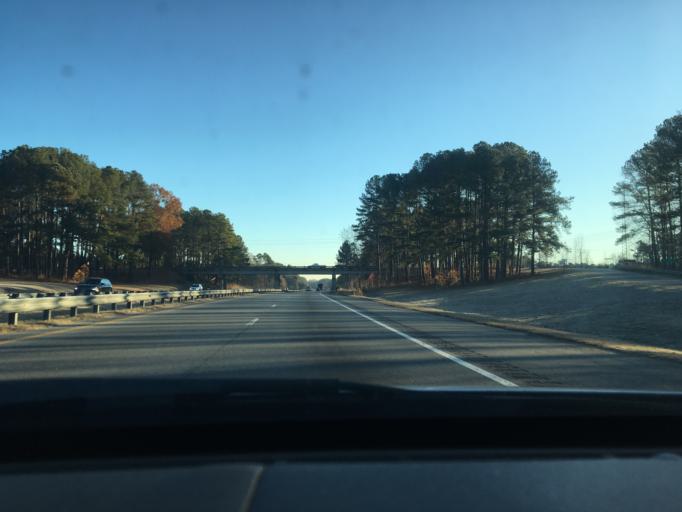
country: US
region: North Carolina
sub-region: Wake County
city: Holly Springs
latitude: 35.6680
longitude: -78.9325
